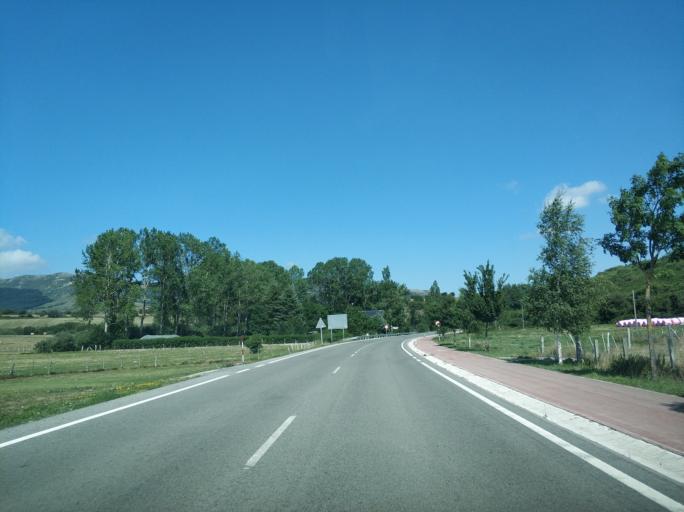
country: ES
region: Cantabria
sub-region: Provincia de Cantabria
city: Villaescusa
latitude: 43.0216
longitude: -4.2334
